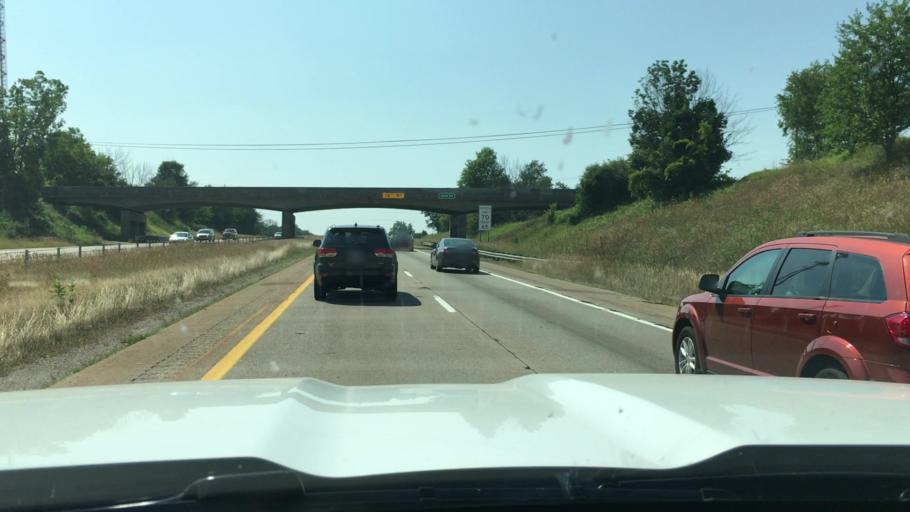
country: US
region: Michigan
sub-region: Ionia County
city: Portland
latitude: 42.8616
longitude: -84.9207
